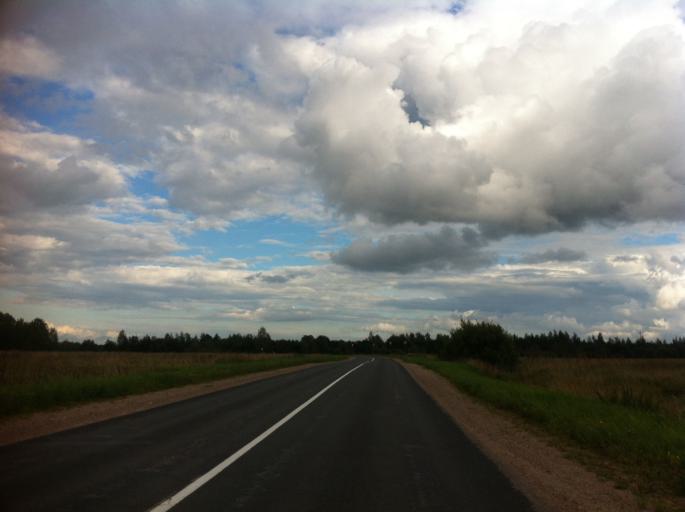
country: RU
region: Pskov
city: Izborsk
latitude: 57.8366
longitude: 27.9954
